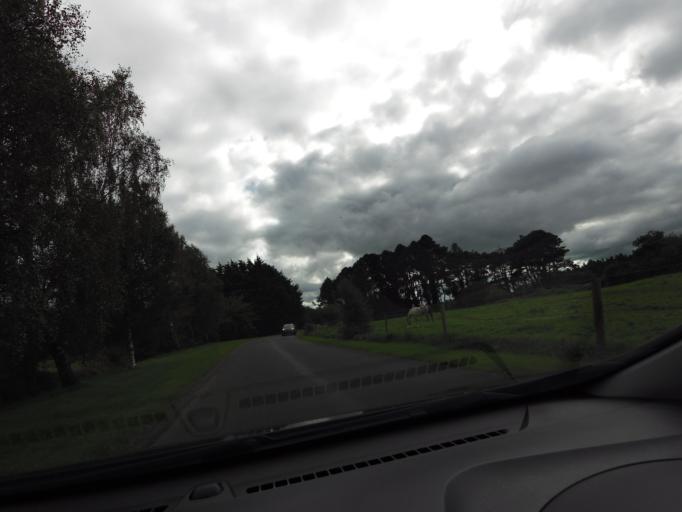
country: IE
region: Leinster
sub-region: Uibh Fhaili
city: Ferbane
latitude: 53.2264
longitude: -7.7288
